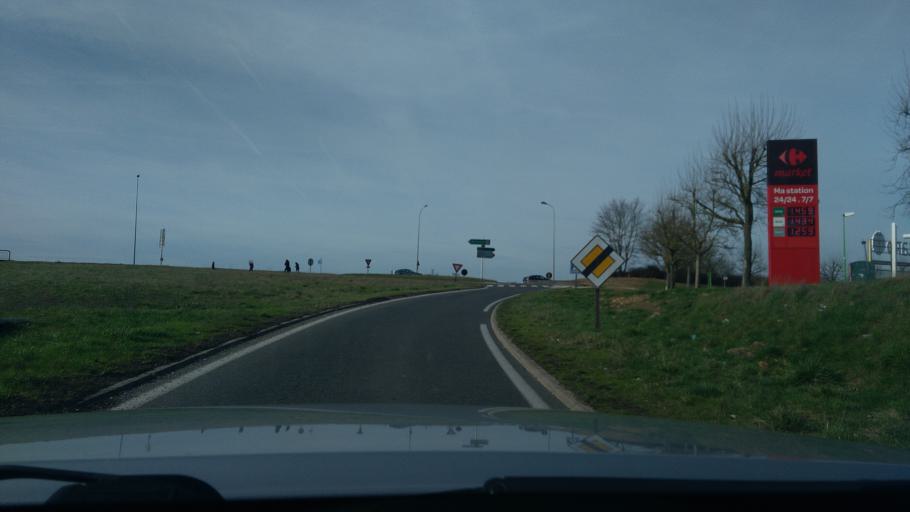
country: FR
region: Ile-de-France
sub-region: Departement de Seine-et-Marne
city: Rubelles
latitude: 48.5523
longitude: 2.6694
